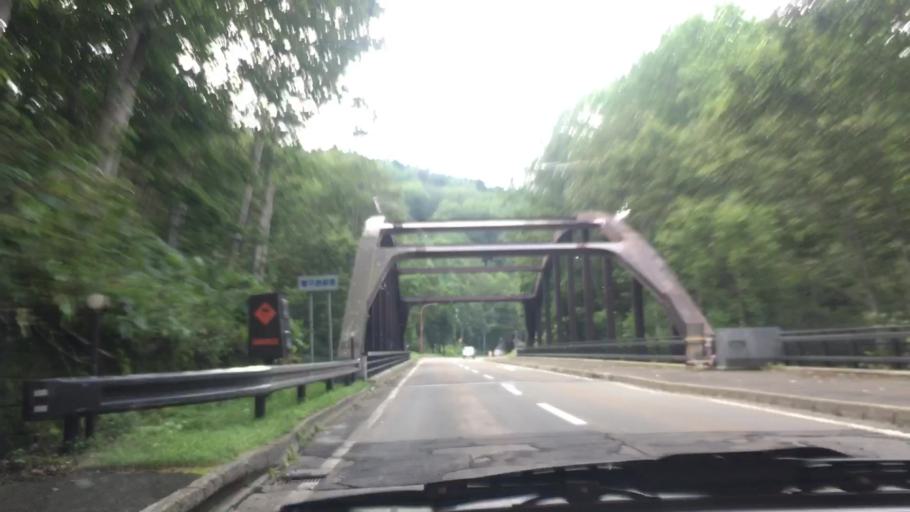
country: JP
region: Hokkaido
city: Otofuke
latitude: 43.3710
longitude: 143.2166
